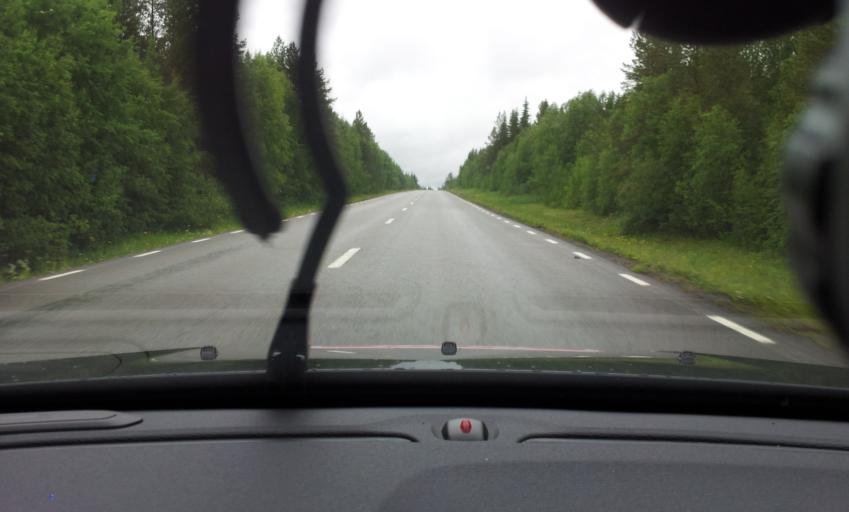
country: SE
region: Jaemtland
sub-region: Krokoms Kommun
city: Krokom
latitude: 63.4224
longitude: 14.4954
